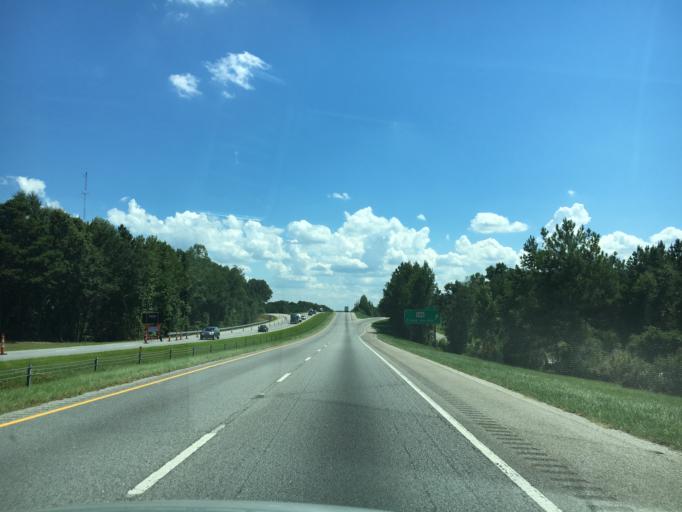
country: US
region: South Carolina
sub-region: Spartanburg County
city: Woodruff
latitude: 34.7033
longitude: -81.9417
